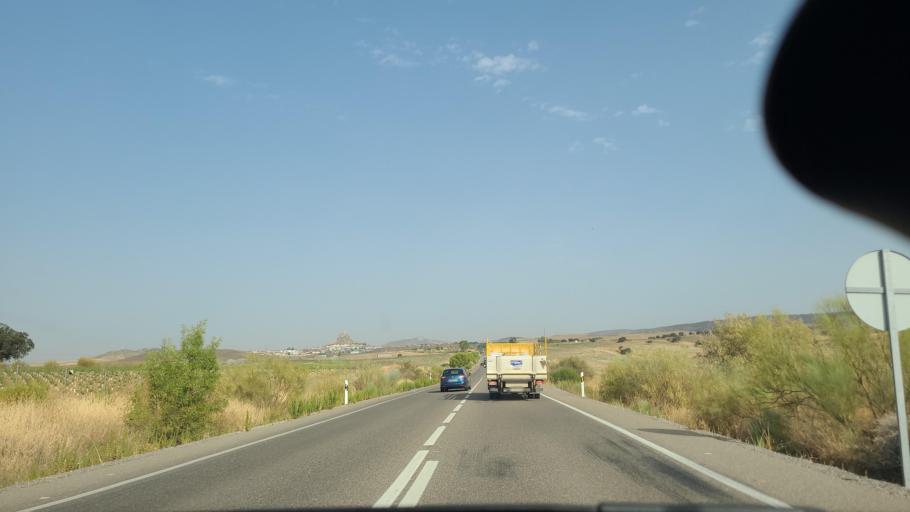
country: ES
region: Andalusia
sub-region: Province of Cordoba
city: Belmez
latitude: 38.2577
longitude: -5.1737
